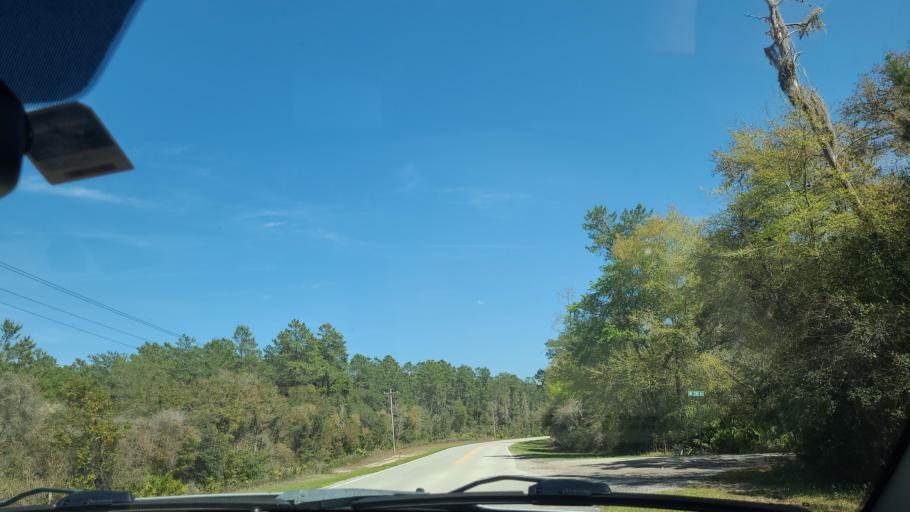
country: US
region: Florida
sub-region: Putnam County
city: Crescent City
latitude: 29.3782
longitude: -81.7581
